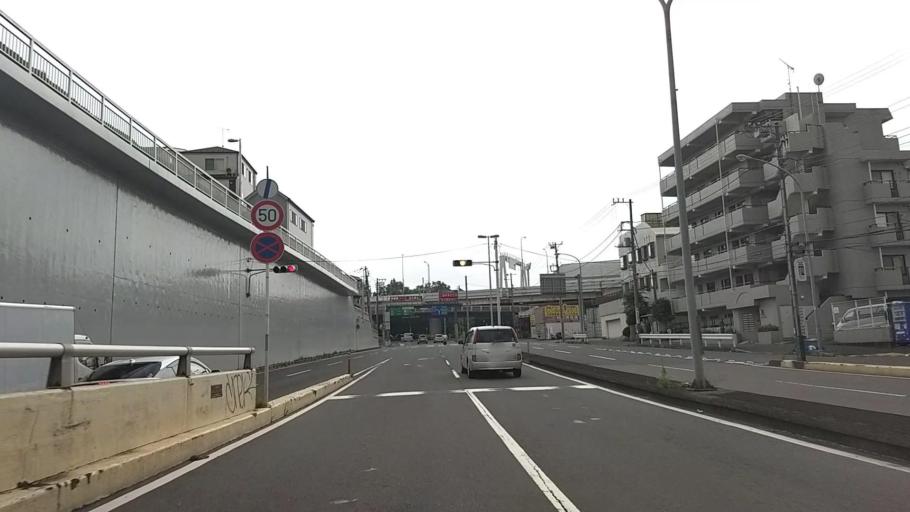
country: JP
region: Kanagawa
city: Yokohama
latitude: 35.4742
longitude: 139.6028
